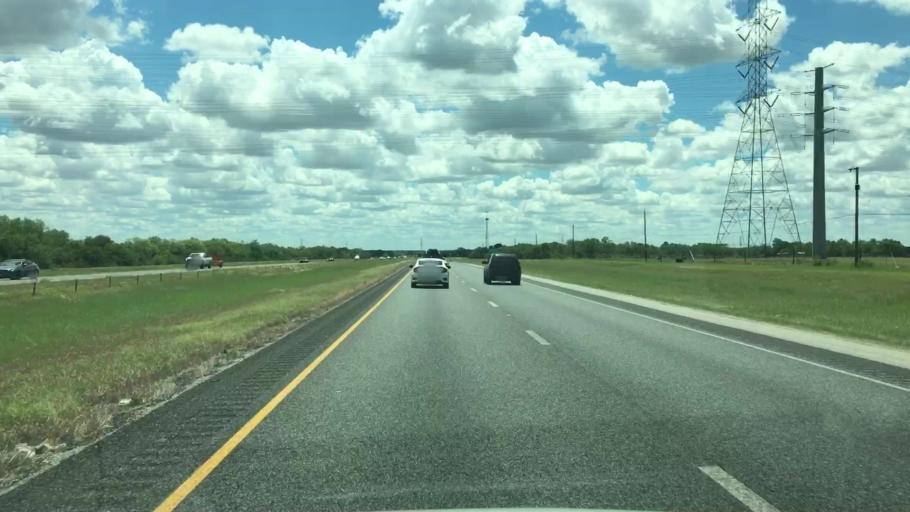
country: US
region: Texas
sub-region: Bexar County
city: Elmendorf
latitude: 29.2696
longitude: -98.3961
